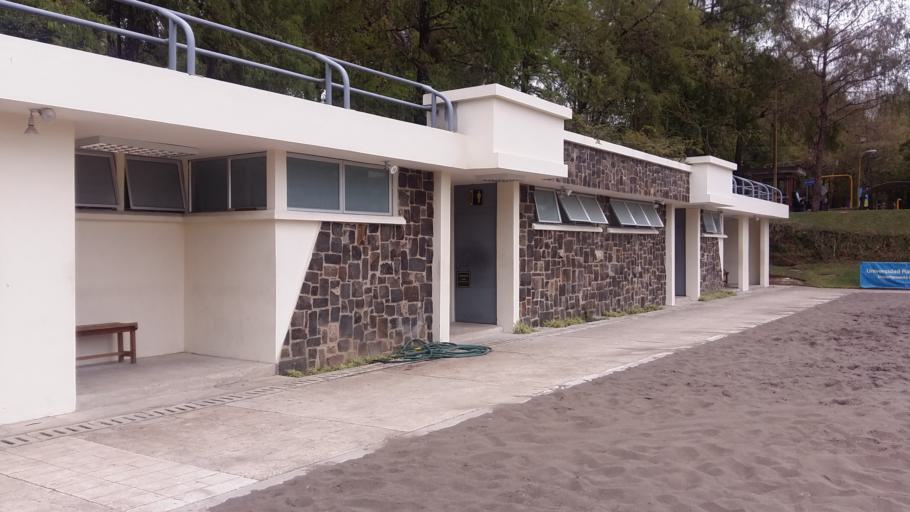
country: GT
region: Guatemala
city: Santa Catarina Pinula
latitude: 14.5979
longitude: -90.4849
